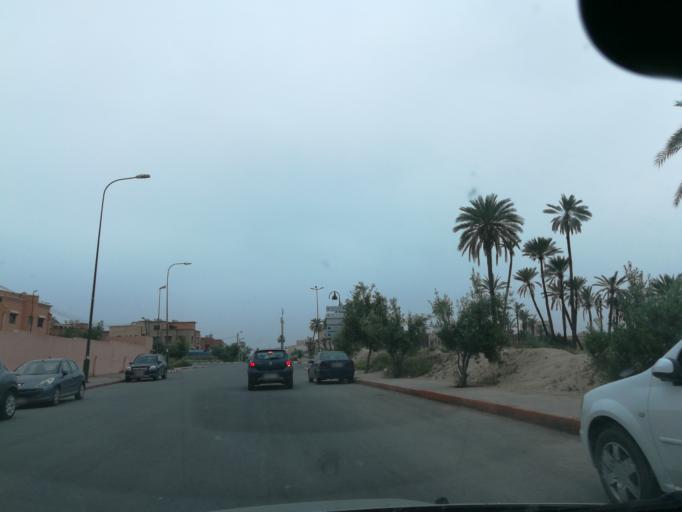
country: MA
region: Marrakech-Tensift-Al Haouz
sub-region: Marrakech
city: Marrakesh
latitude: 31.6683
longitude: -7.9966
